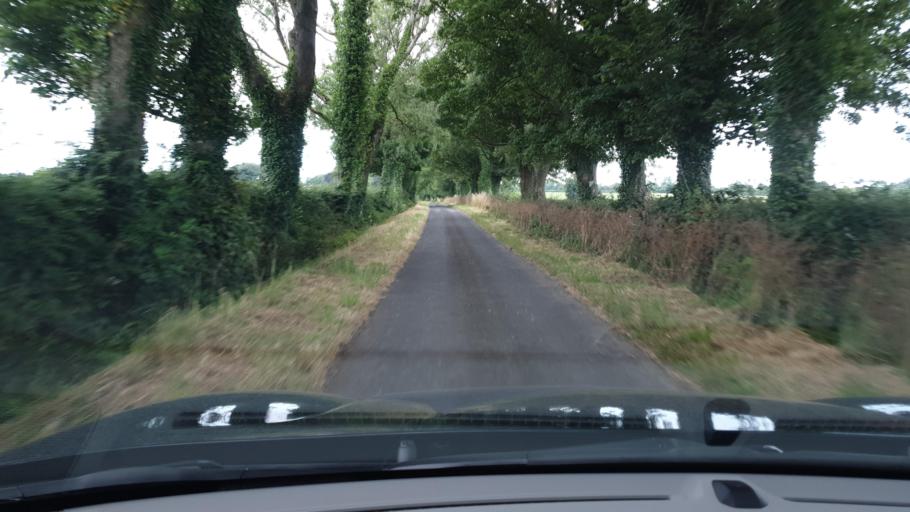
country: IE
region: Leinster
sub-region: An Mhi
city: Ashbourne
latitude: 53.5452
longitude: -6.3875
